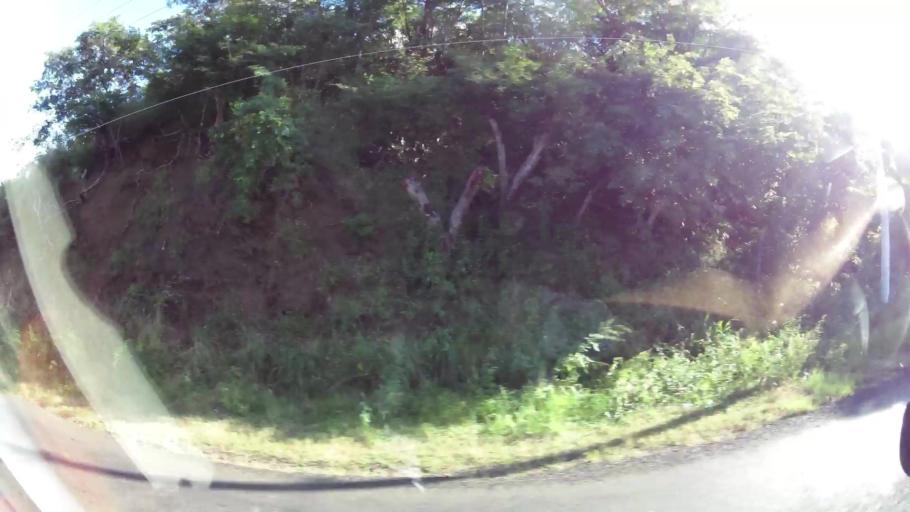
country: CR
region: Guanacaste
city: Sardinal
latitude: 10.5806
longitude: -85.6677
